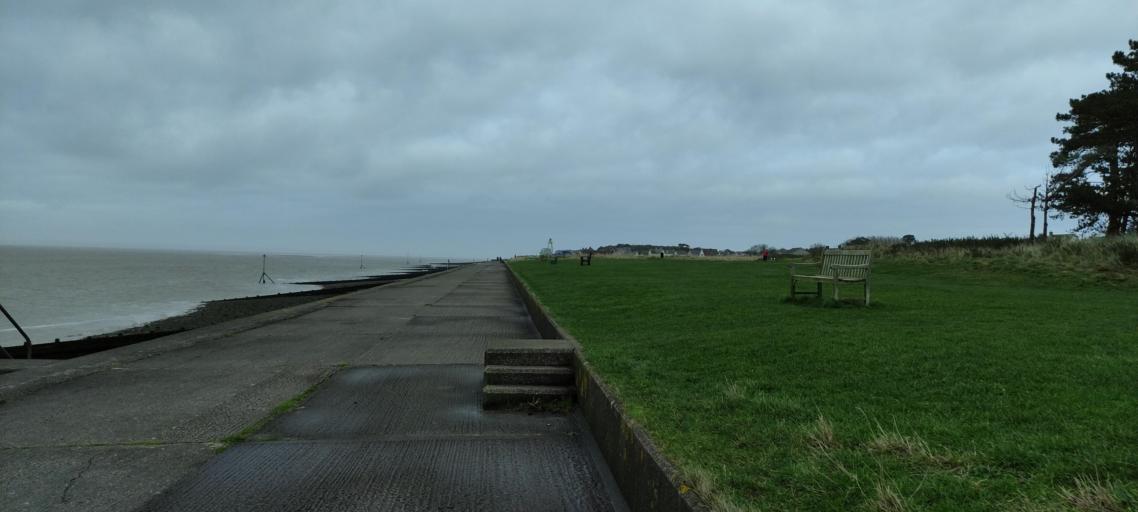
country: GB
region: England
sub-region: Cumbria
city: Silloth
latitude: 54.8757
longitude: -3.3851
